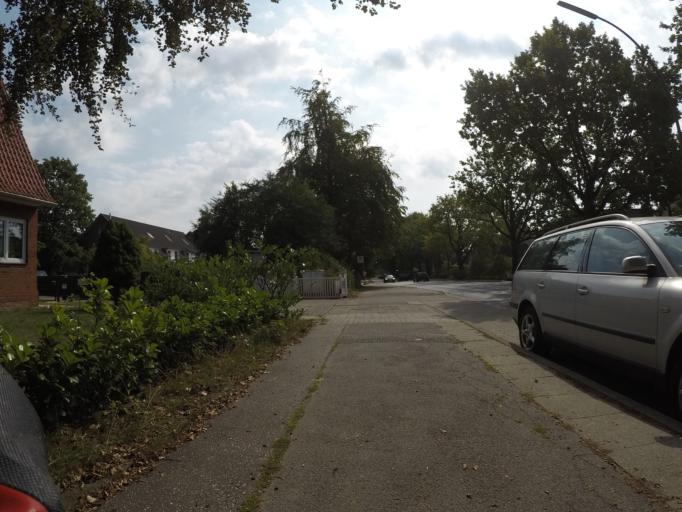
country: DE
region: Hamburg
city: Poppenbuettel
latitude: 53.6718
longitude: 10.0603
